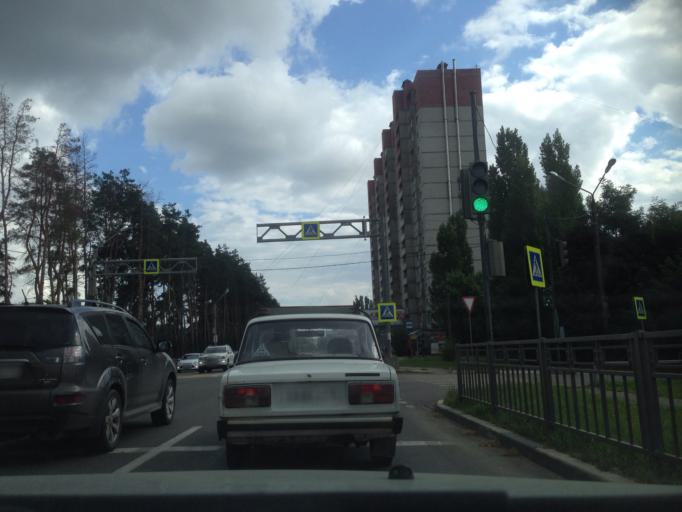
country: RU
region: Voronezj
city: Podgornoye
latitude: 51.7265
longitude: 39.1873
